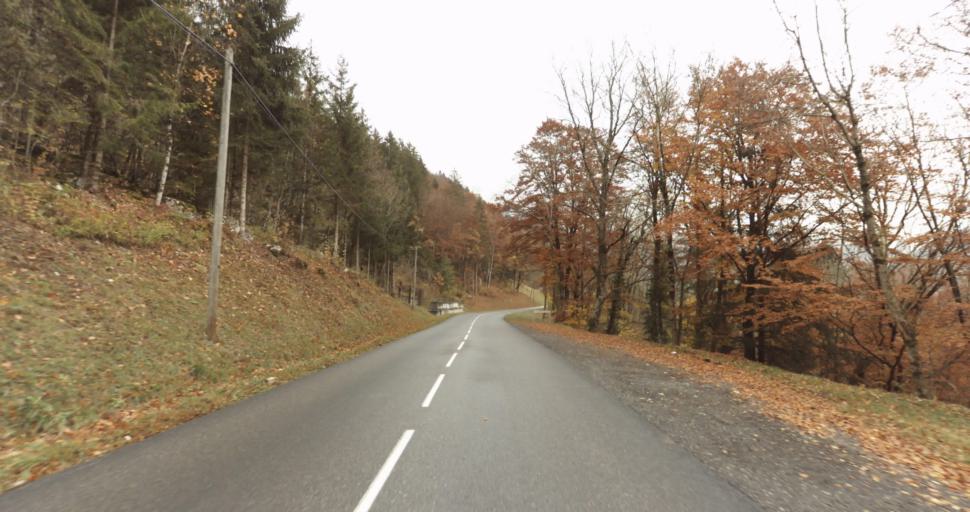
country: FR
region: Rhone-Alpes
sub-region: Departement de la Haute-Savoie
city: Thorens-Glieres
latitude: 45.9888
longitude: 6.2681
